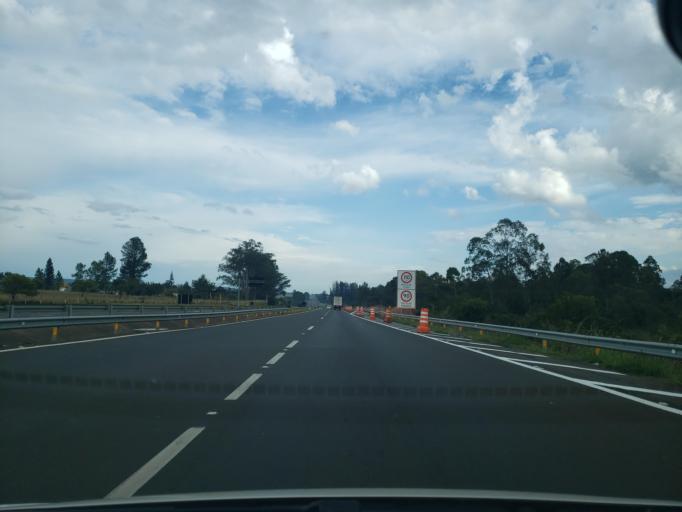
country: BR
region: Sao Paulo
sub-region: Itirapina
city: Itirapina
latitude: -22.2638
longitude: -47.9038
